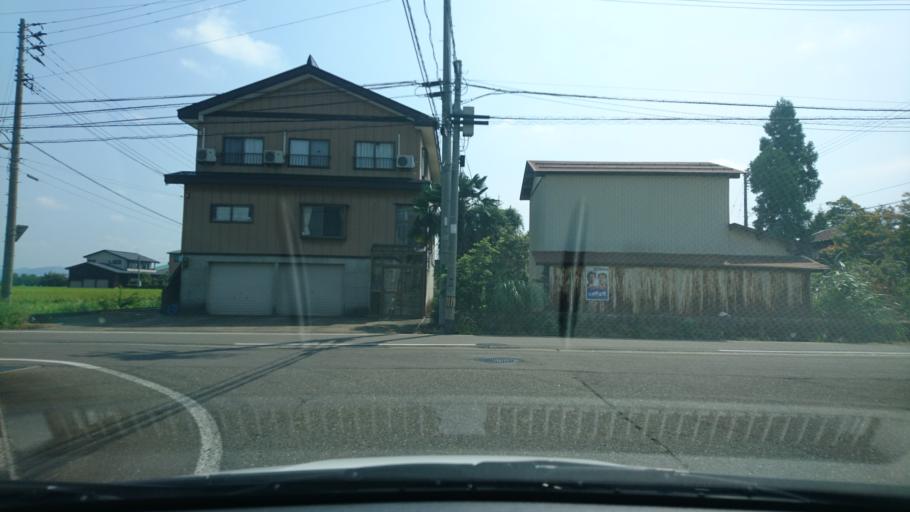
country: JP
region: Niigata
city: Arai
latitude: 37.0461
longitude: 138.2639
